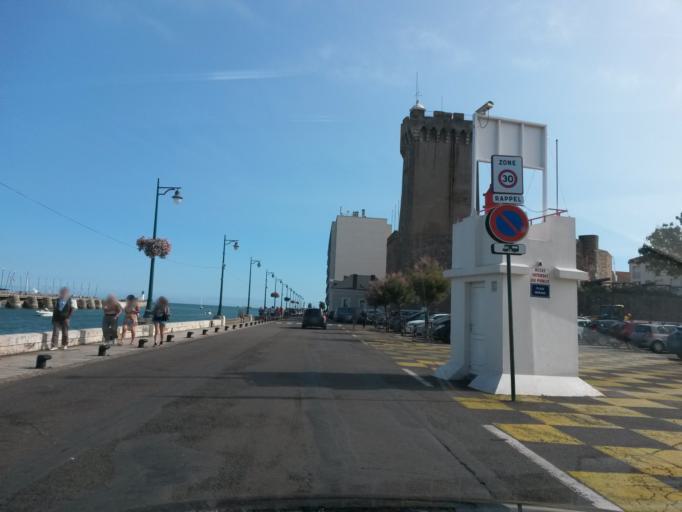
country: FR
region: Pays de la Loire
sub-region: Departement de la Vendee
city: Les Sables-d'Olonne
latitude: 46.4945
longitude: -1.7959
